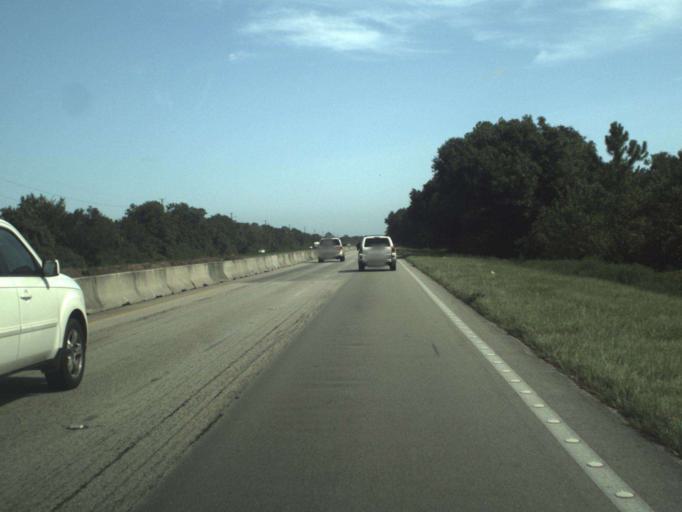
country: US
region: Florida
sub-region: Indian River County
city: West Vero Corridor
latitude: 27.6868
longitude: -80.5354
